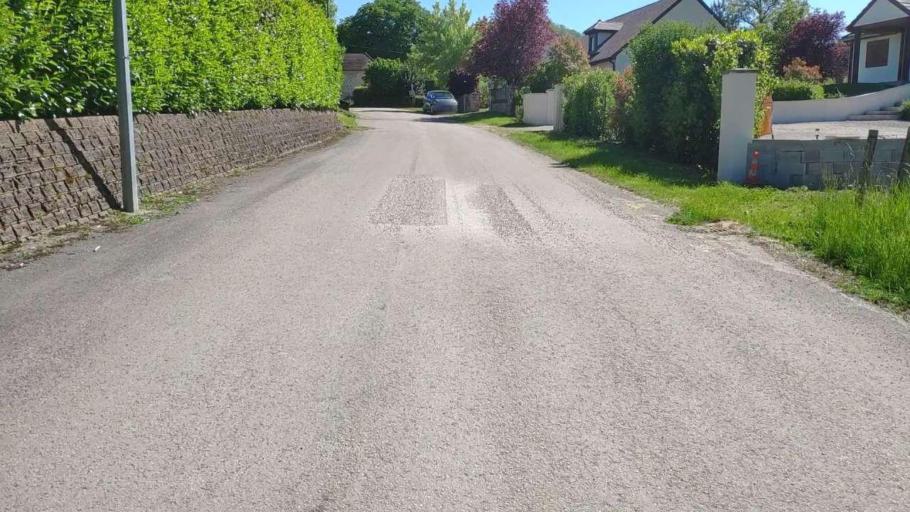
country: FR
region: Franche-Comte
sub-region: Departement du Jura
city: Perrigny
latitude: 46.7312
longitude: 5.5826
